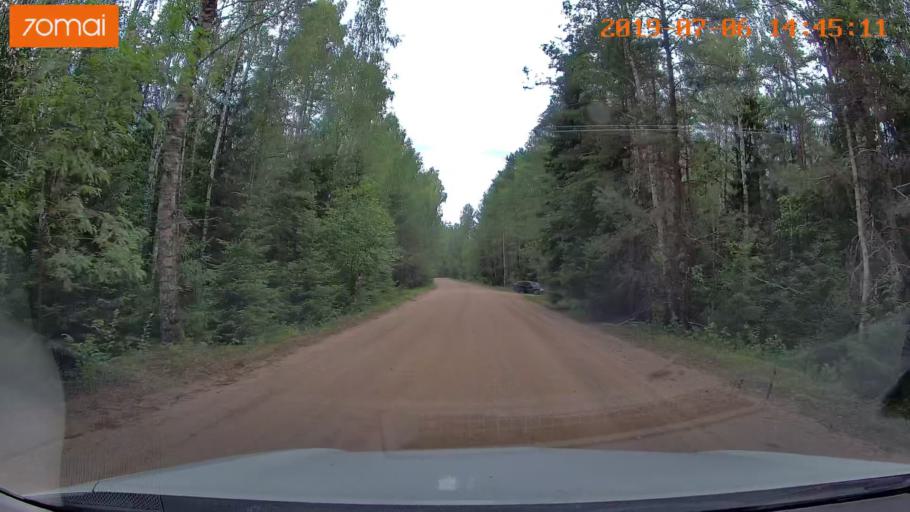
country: BY
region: Minsk
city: Ivyanyets
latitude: 53.9697
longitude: 26.6887
